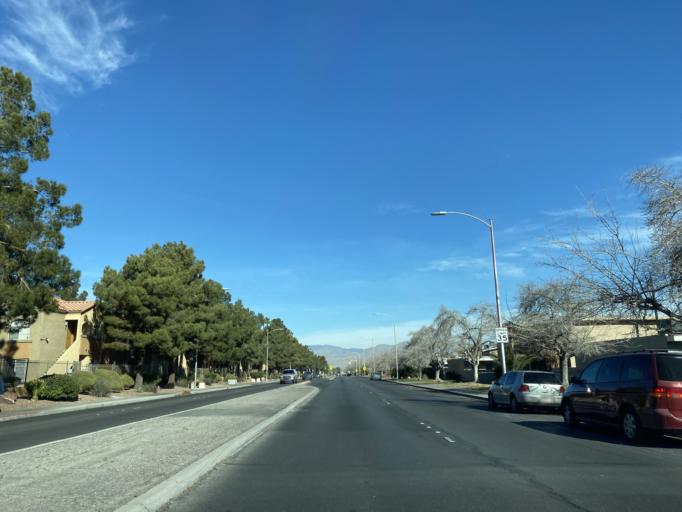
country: US
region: Nevada
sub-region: Clark County
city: Spring Valley
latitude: 36.1821
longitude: -115.2238
